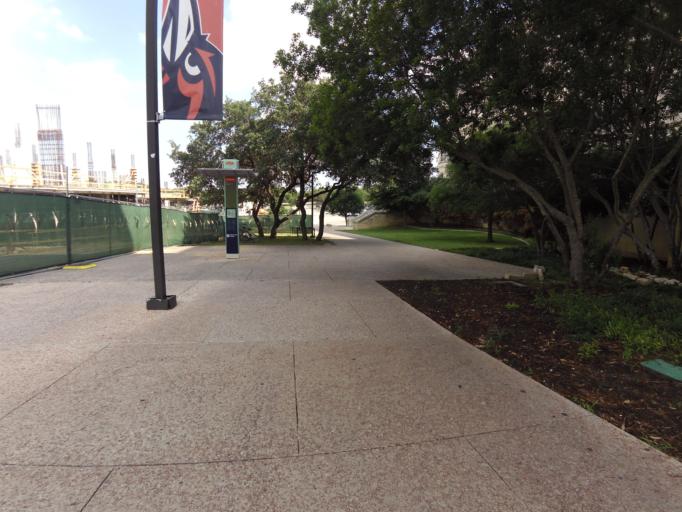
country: US
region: Texas
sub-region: Bexar County
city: Shavano Park
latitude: 29.5819
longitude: -98.6172
